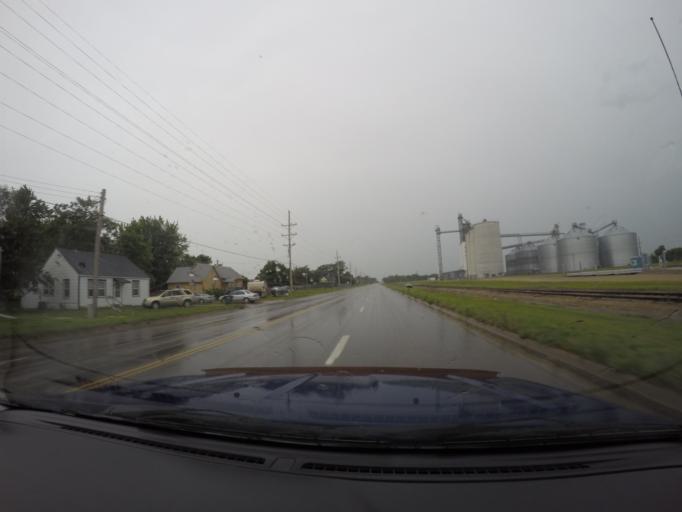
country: US
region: Kansas
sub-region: Cloud County
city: Concordia
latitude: 39.5736
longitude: -97.6738
